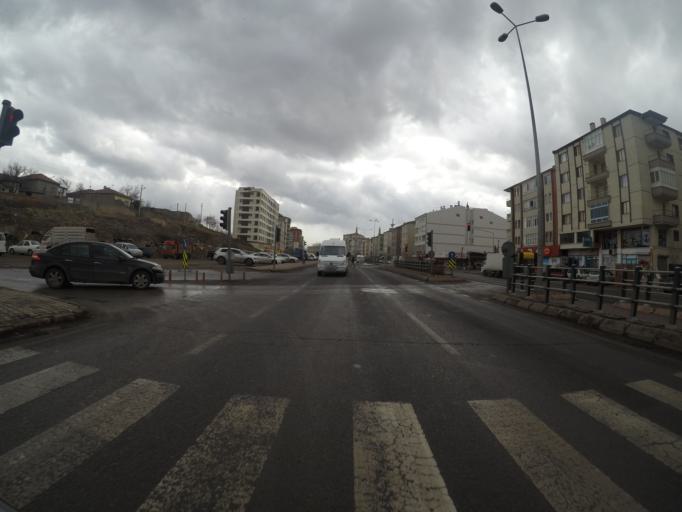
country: TR
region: Kayseri
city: Melikgazi
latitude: 38.7560
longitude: 35.4678
